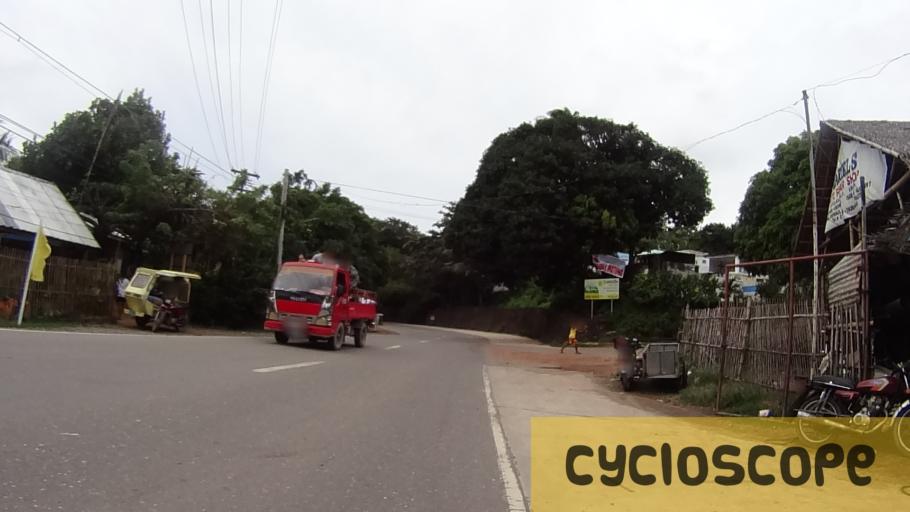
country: PH
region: Western Visayas
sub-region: Province of Aklan
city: Caticlan
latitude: 11.9324
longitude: 121.9565
